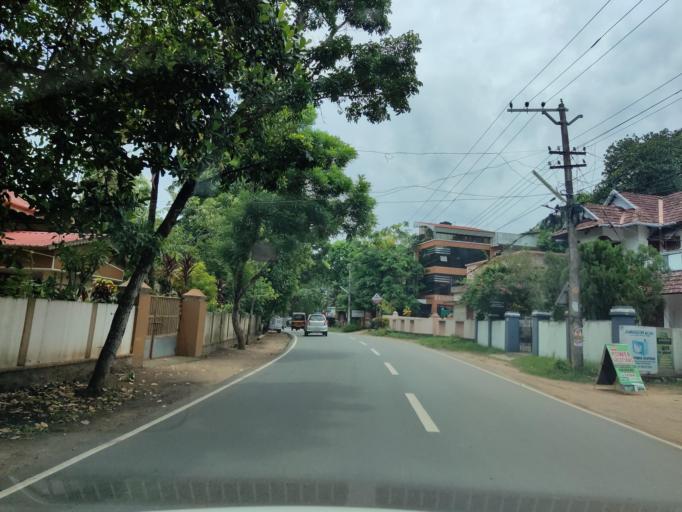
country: IN
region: Kerala
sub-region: Pattanamtitta
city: Adur
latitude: 9.2277
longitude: 76.6656
